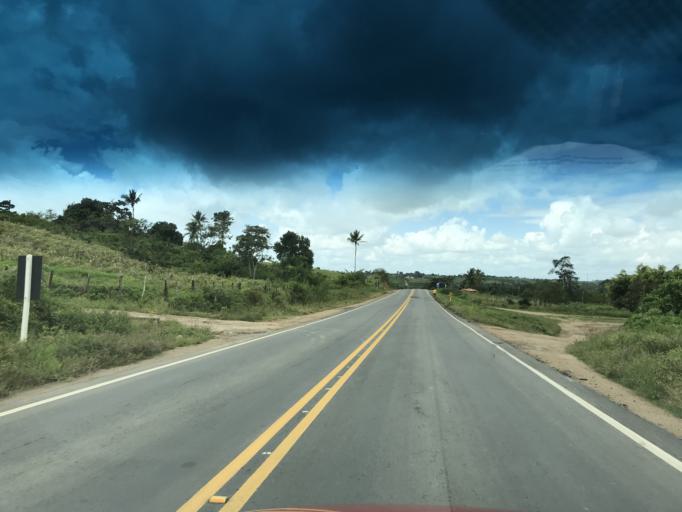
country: BR
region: Bahia
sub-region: Conceicao Do Almeida
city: Conceicao do Almeida
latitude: -12.7038
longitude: -39.2354
